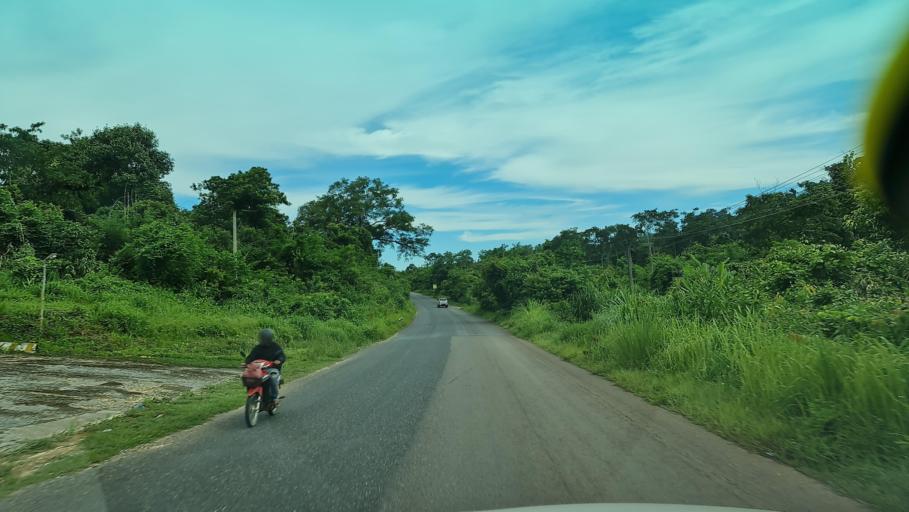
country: TH
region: Nakhon Phanom
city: Ban Phaeng
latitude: 17.9791
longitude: 104.3210
